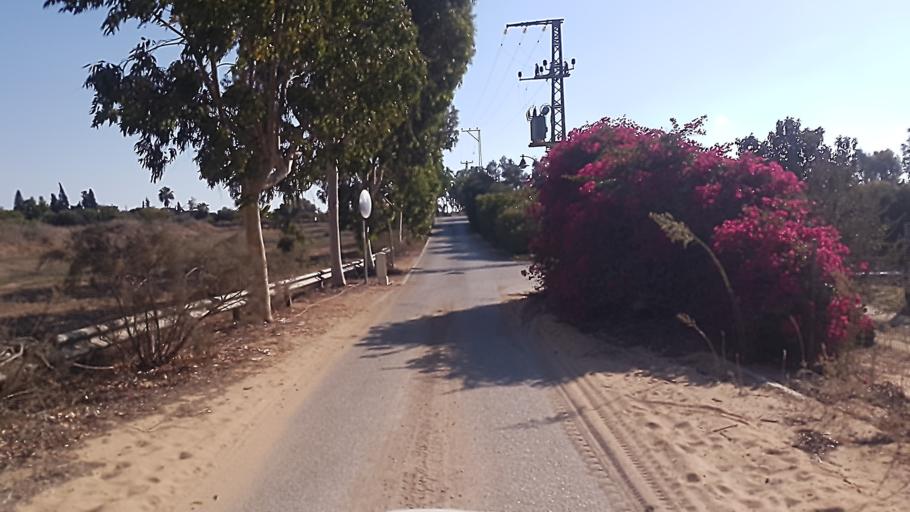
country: IL
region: Central District
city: Kfar Saba
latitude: 32.2036
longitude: 34.9146
